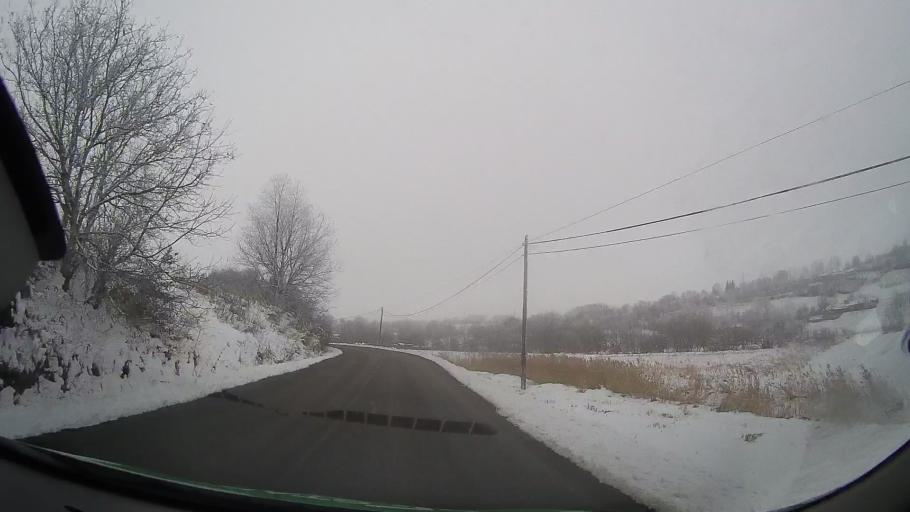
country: RO
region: Bacau
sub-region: Comuna Oncesti
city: Oncesti
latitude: 46.4743
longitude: 27.2556
